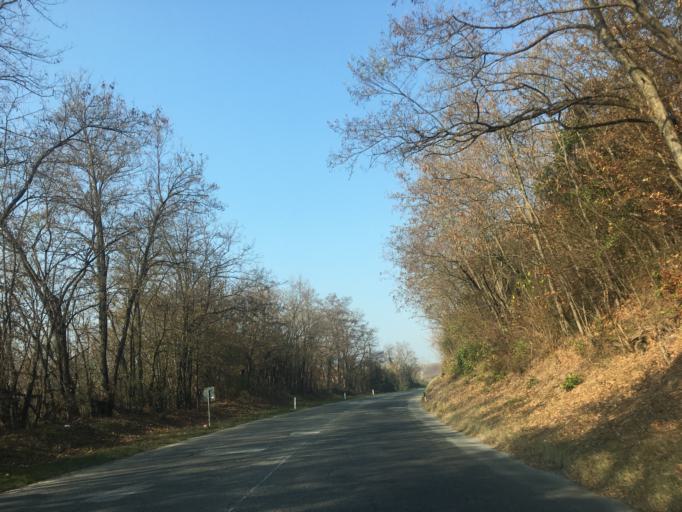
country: XK
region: Pec
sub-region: Komuna e Pejes
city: Kosuriq
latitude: 42.6387
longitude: 20.4289
